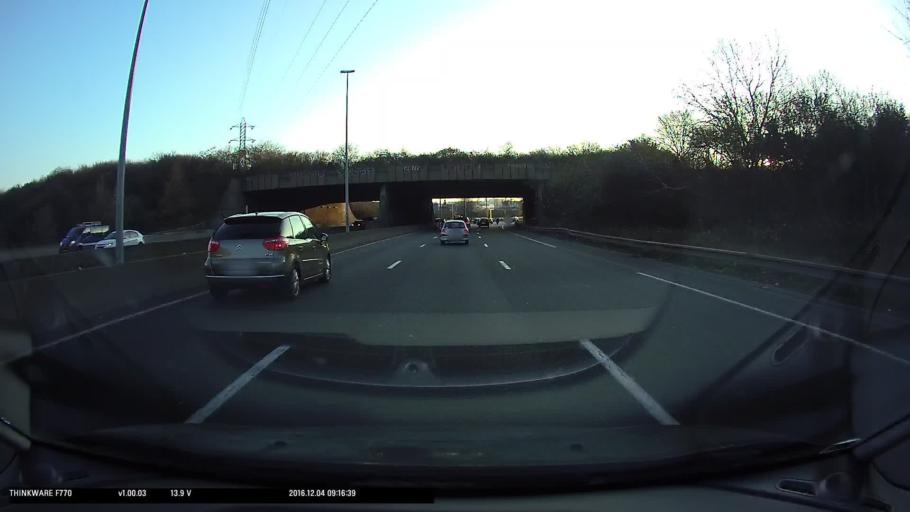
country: FR
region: Ile-de-France
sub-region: Departement des Hauts-de-Seine
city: Villeneuve-la-Garenne
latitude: 48.9383
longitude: 2.3124
